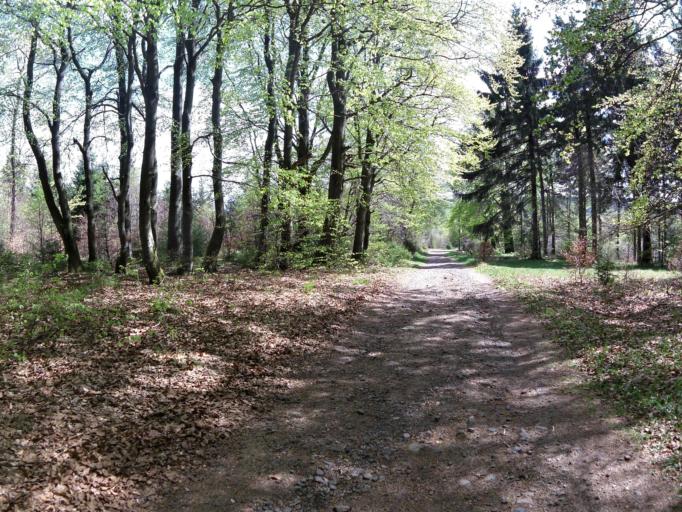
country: DE
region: Thuringia
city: Friedrichroda
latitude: 50.8181
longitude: 10.5414
